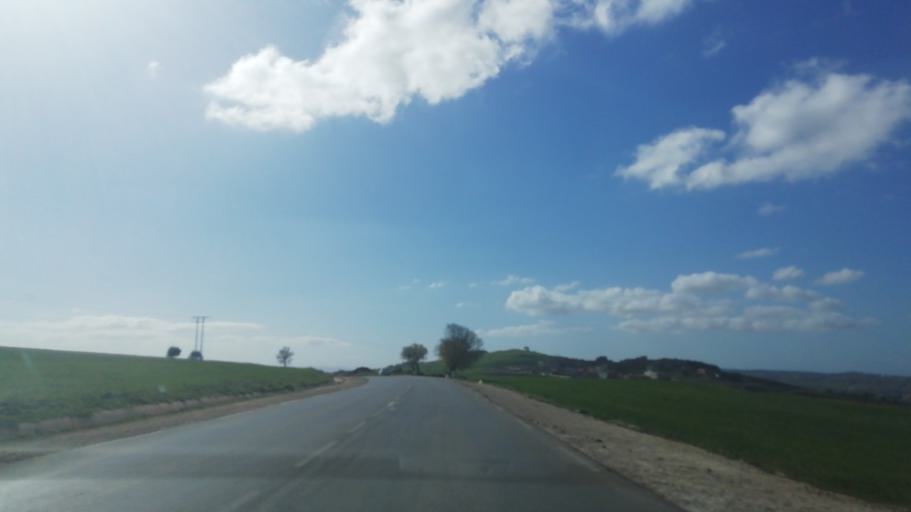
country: DZ
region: Relizane
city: Relizane
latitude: 36.0917
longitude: 0.4462
